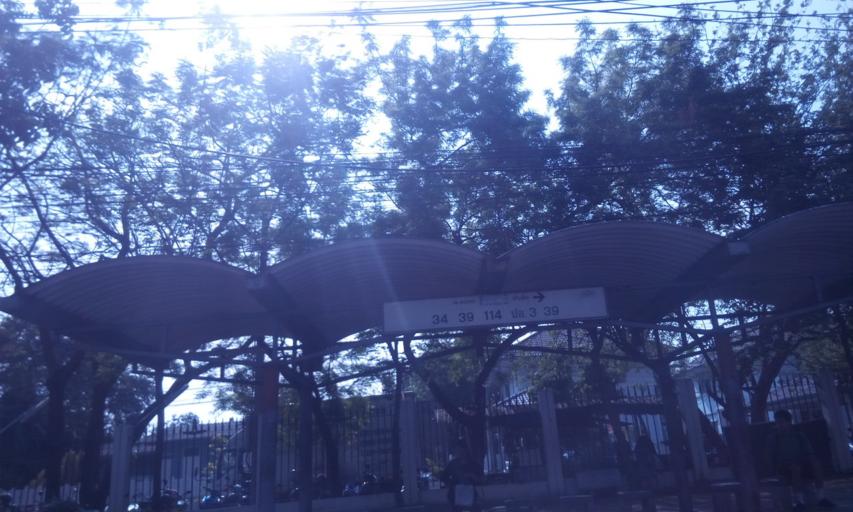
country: TH
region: Bangkok
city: Sai Mai
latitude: 13.9162
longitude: 100.6208
